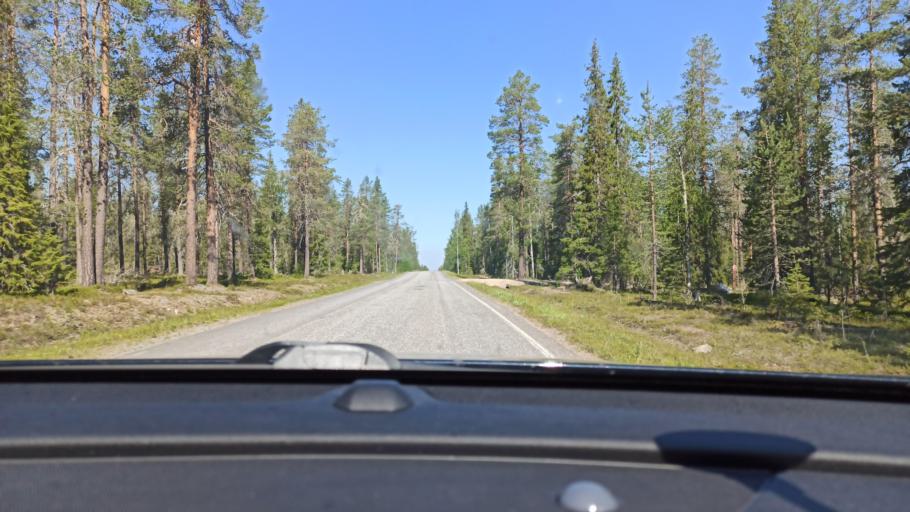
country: FI
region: Lapland
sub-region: Tunturi-Lappi
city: Kolari
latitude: 67.6727
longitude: 24.1476
